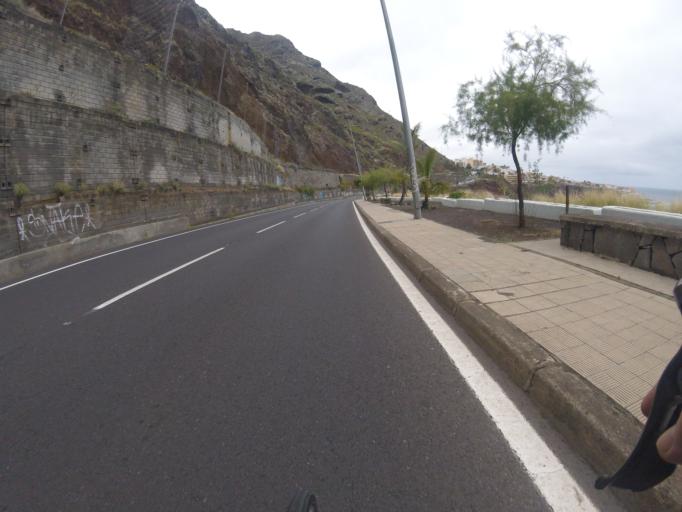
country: ES
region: Canary Islands
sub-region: Provincia de Santa Cruz de Tenerife
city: Tegueste
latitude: 28.5585
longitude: -16.3324
